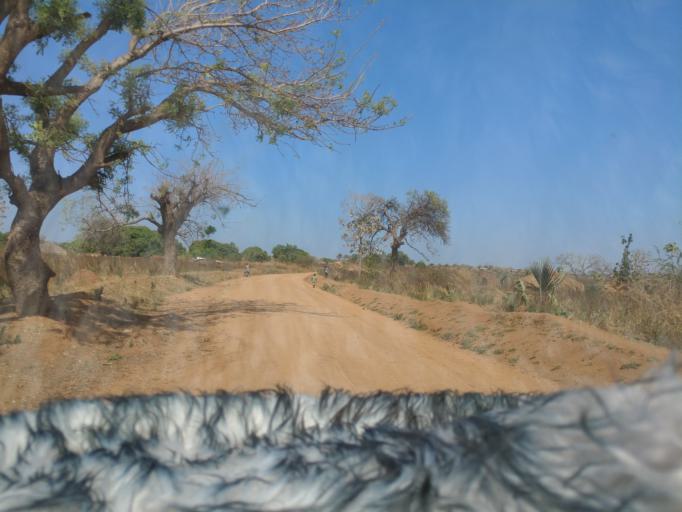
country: UG
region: Northern Region
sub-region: Yumbe District
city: Yumbe
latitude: 3.3888
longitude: 31.3270
